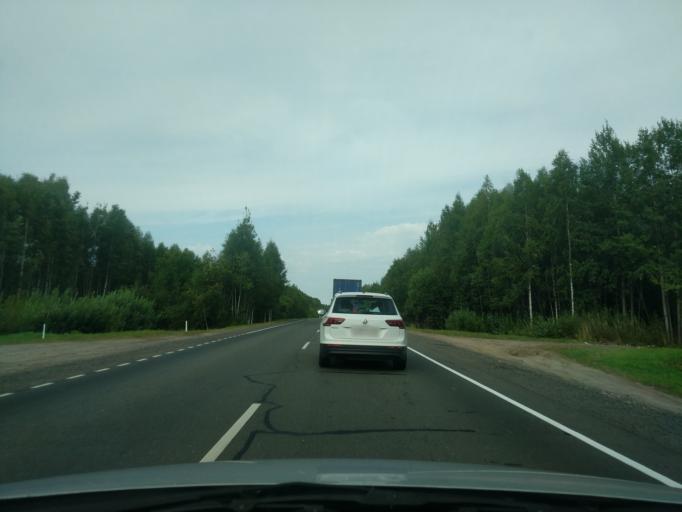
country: RU
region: Kirov
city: Leninskoye
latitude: 58.2853
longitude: 47.2476
